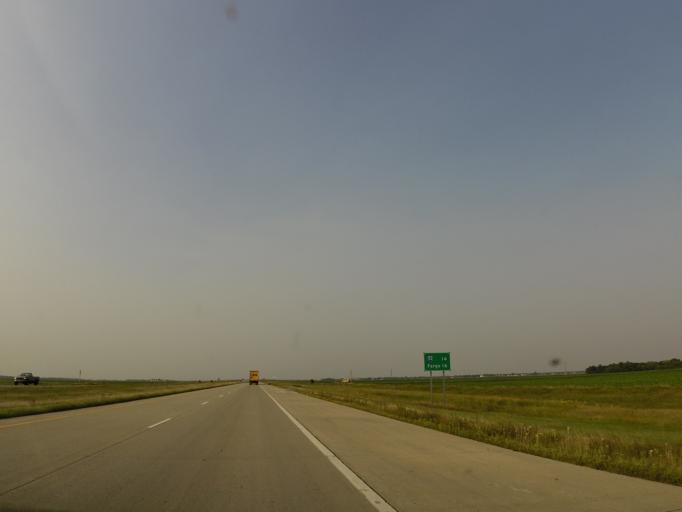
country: US
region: North Dakota
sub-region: Cass County
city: Horace
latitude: 46.6422
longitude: -96.8314
